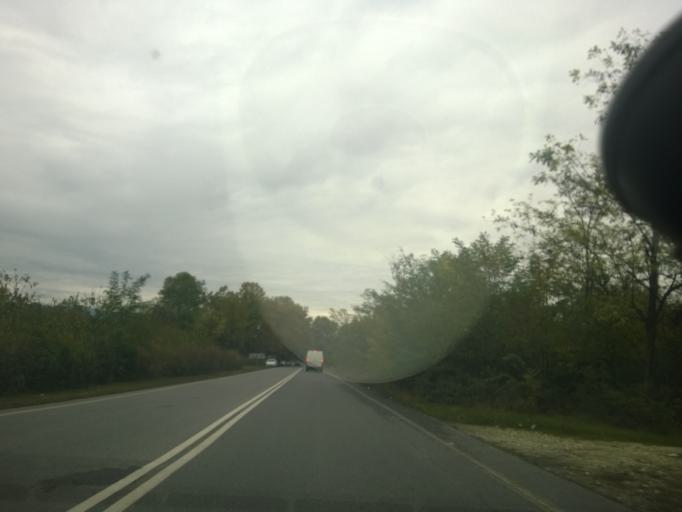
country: GR
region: Central Macedonia
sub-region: Nomos Pellis
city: Loutraki
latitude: 40.9709
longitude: 21.9870
